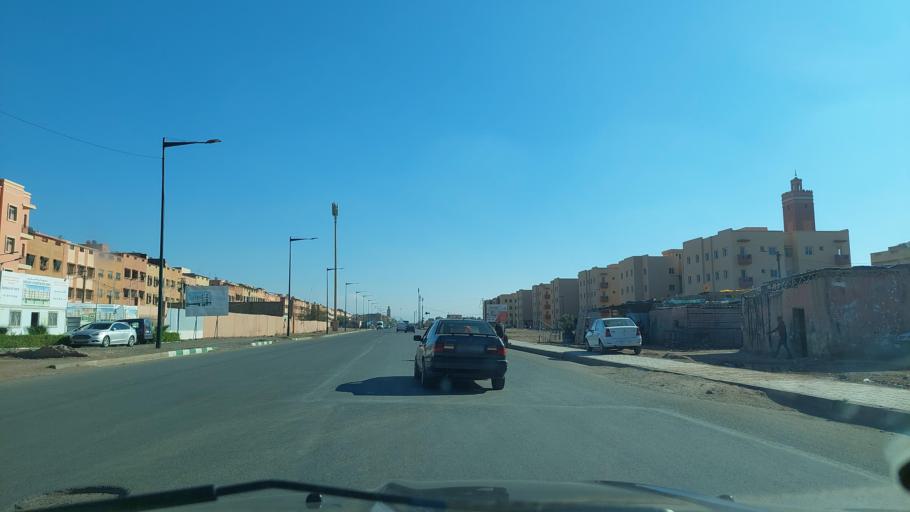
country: MA
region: Marrakech-Tensift-Al Haouz
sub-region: Marrakech
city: Marrakesh
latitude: 31.6265
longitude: -8.0709
